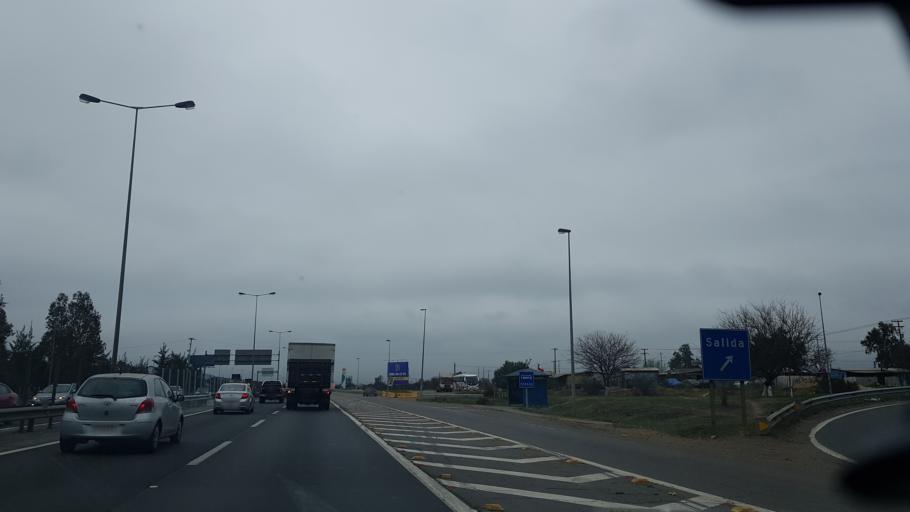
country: CL
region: Santiago Metropolitan
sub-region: Provincia de Santiago
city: Lo Prado
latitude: -33.4394
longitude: -70.8345
